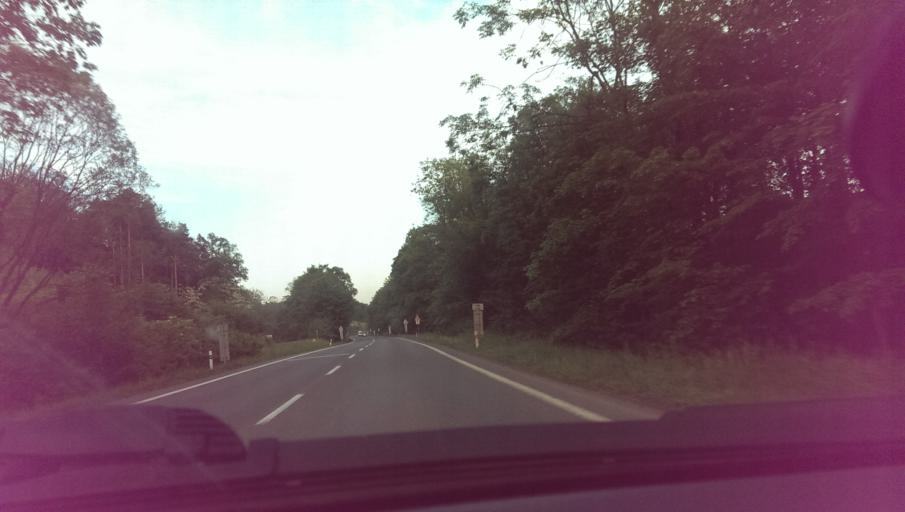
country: CZ
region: Zlin
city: Zasova
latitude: 49.4741
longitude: 18.0122
